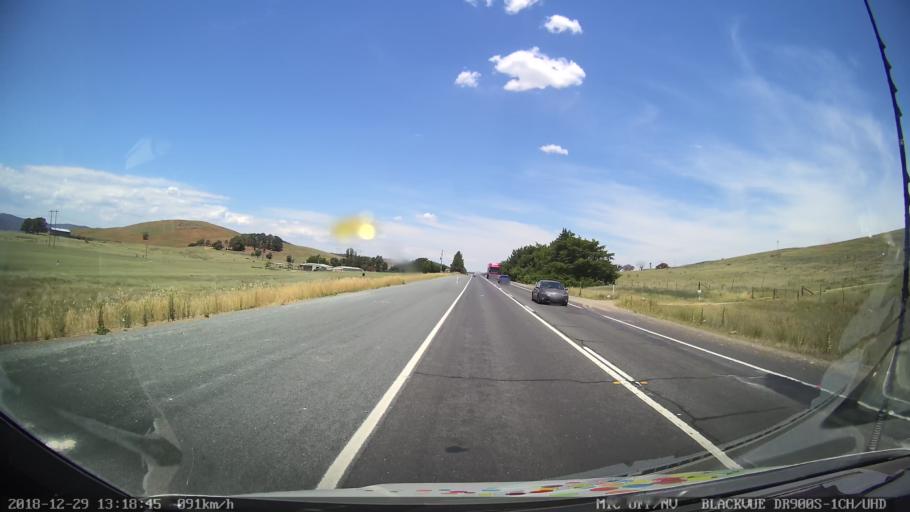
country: AU
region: Australian Capital Territory
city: Macarthur
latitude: -35.7557
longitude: 149.1610
